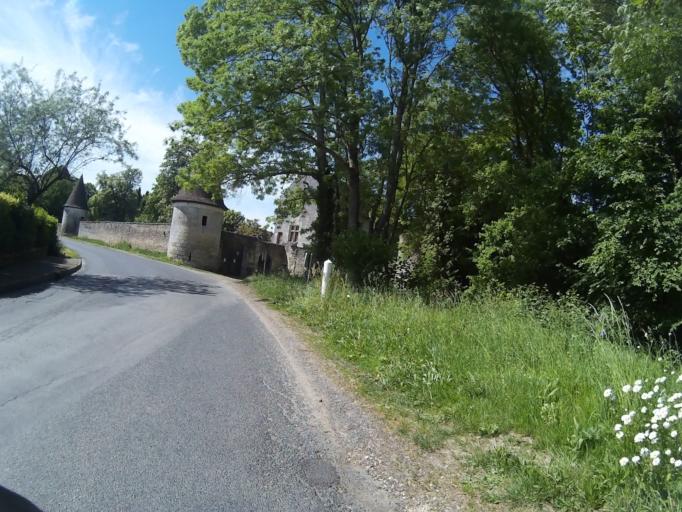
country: FR
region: Centre
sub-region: Departement du Loir-et-Cher
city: Lunay
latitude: 47.8115
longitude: 0.9563
